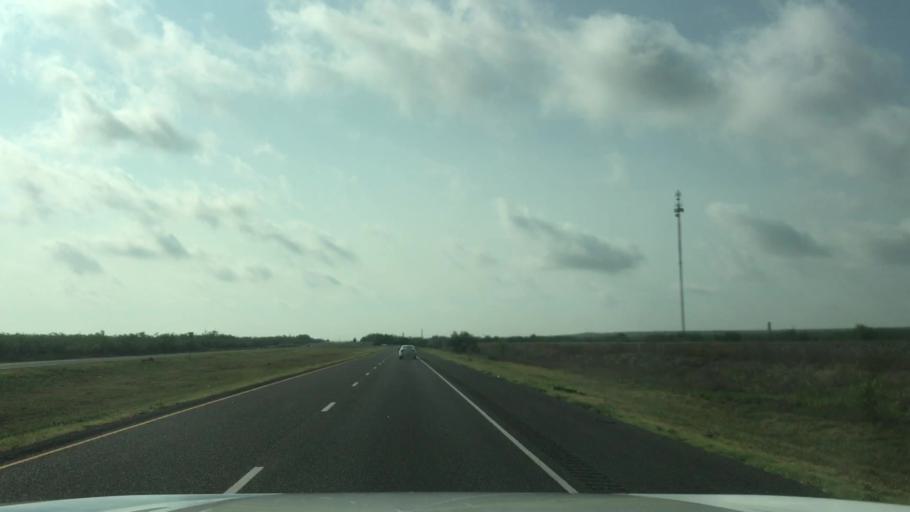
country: US
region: Texas
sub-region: Scurry County
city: Snyder
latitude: 32.8614
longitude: -101.0260
